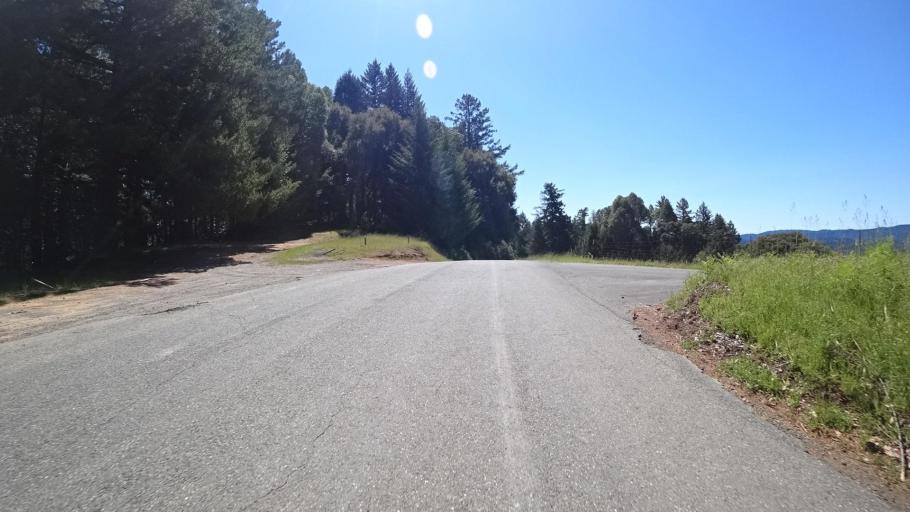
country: US
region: California
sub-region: Humboldt County
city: Redway
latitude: 40.1283
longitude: -123.9746
